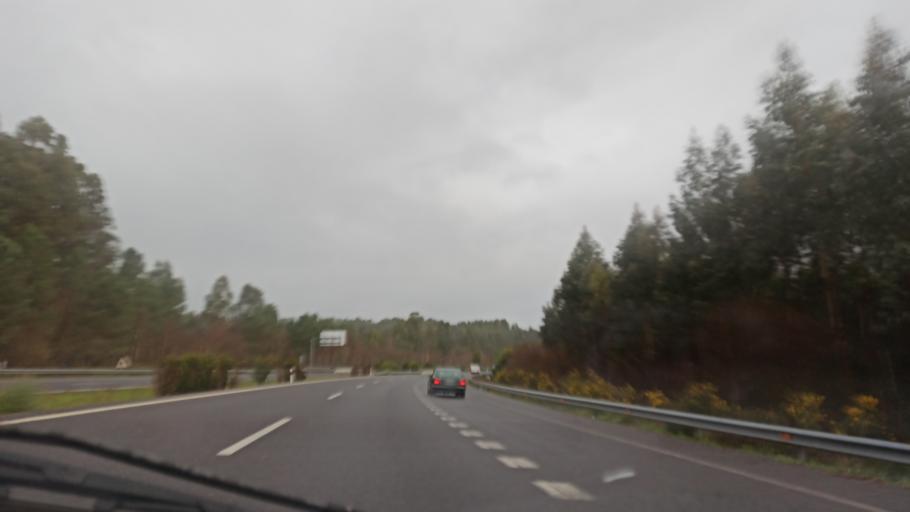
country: ES
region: Galicia
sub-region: Provincia da Coruna
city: Abegondo
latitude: 43.2532
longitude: -8.2945
